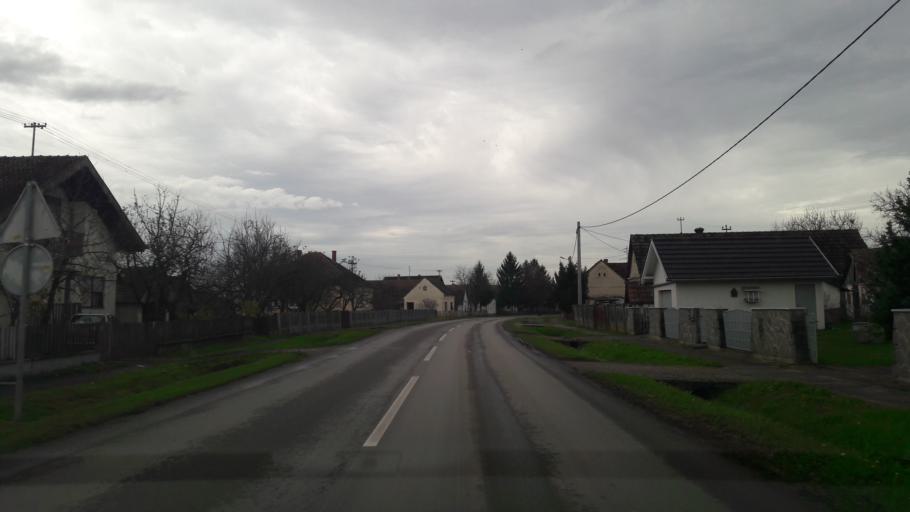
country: HR
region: Osjecko-Baranjska
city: Velimirovac
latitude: 45.5358
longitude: 18.0821
